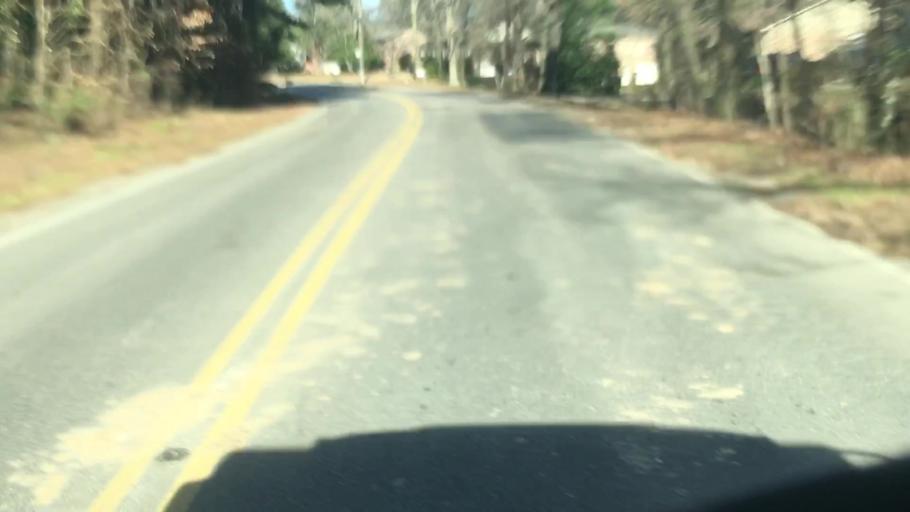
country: US
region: Alabama
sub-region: Shelby County
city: Meadowbrook
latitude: 33.4172
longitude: -86.7391
